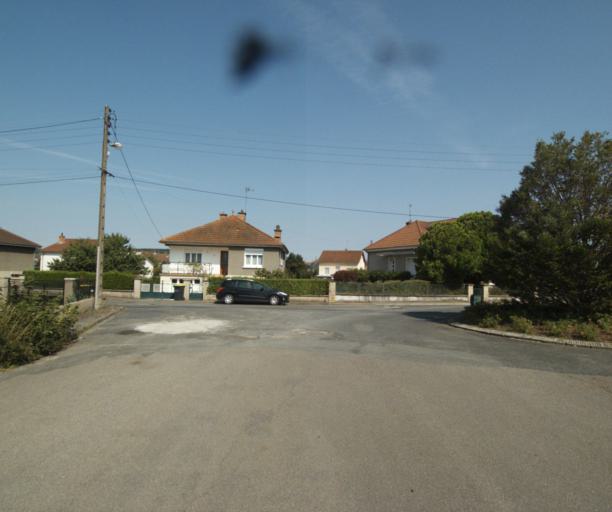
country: FR
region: Bourgogne
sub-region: Departement de Saone-et-Loire
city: Gueugnon
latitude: 46.5979
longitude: 4.0553
